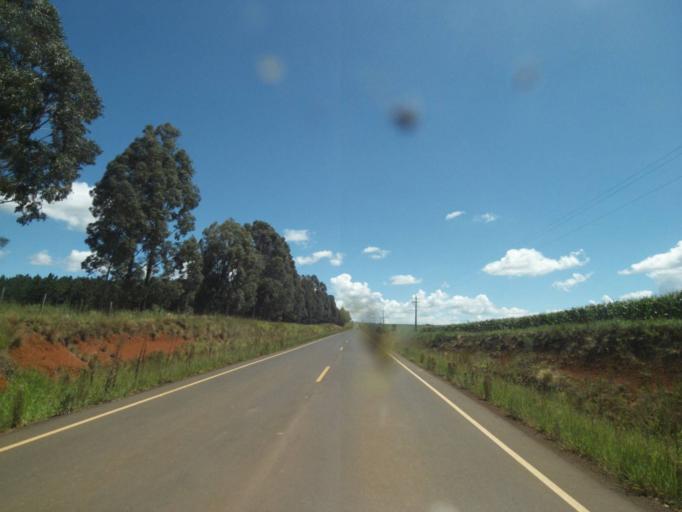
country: BR
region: Parana
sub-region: Pinhao
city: Pinhao
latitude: -25.8261
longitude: -52.0167
